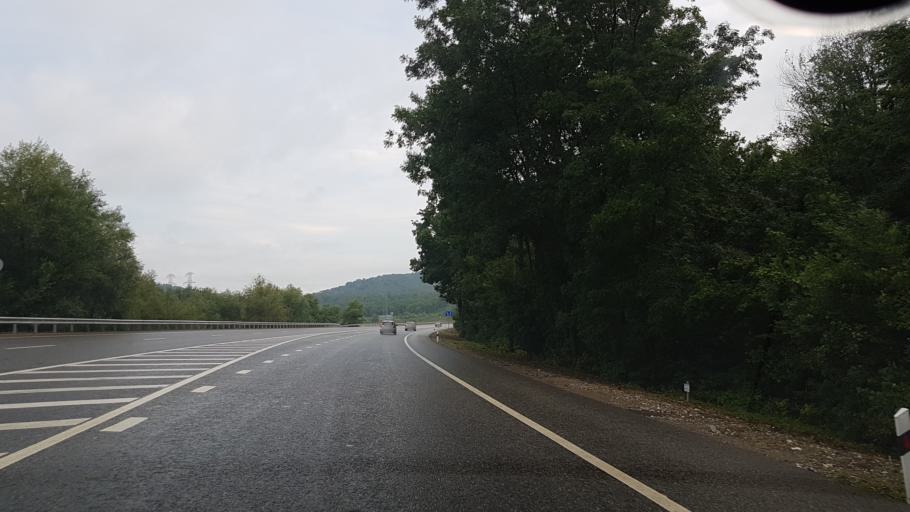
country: RU
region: Krasnodarskiy
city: Dzhubga
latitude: 44.4042
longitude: 38.7364
